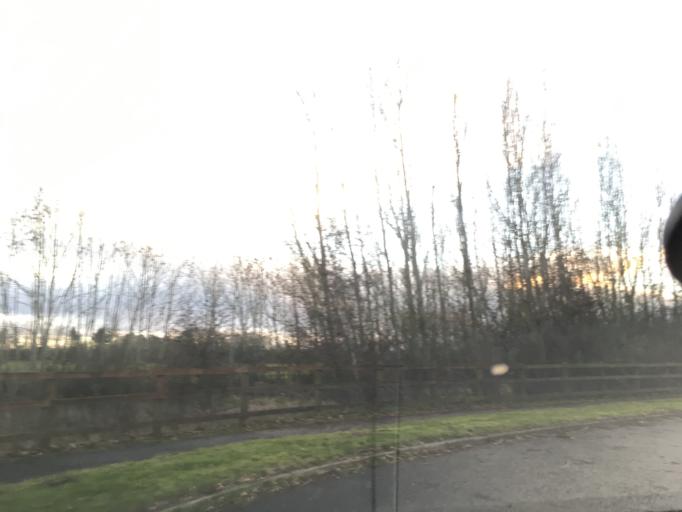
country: GB
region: Scotland
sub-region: Midlothian
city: Loanhead
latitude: 55.8617
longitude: -3.1875
